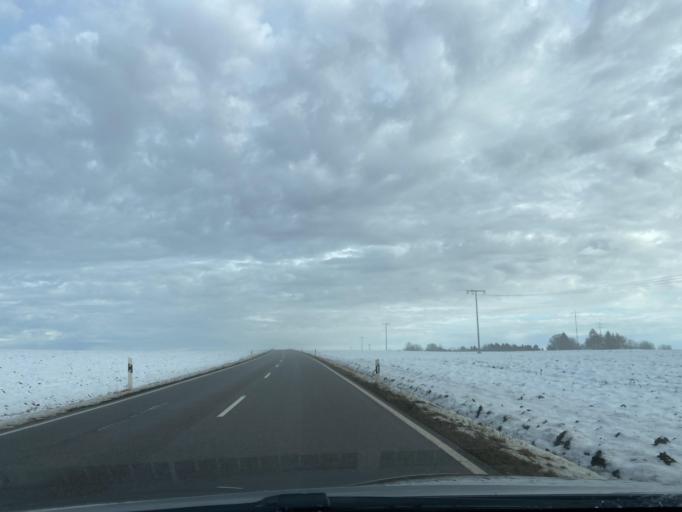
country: DE
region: Baden-Wuerttemberg
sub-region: Tuebingen Region
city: Hettingen
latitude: 48.1798
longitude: 9.2547
